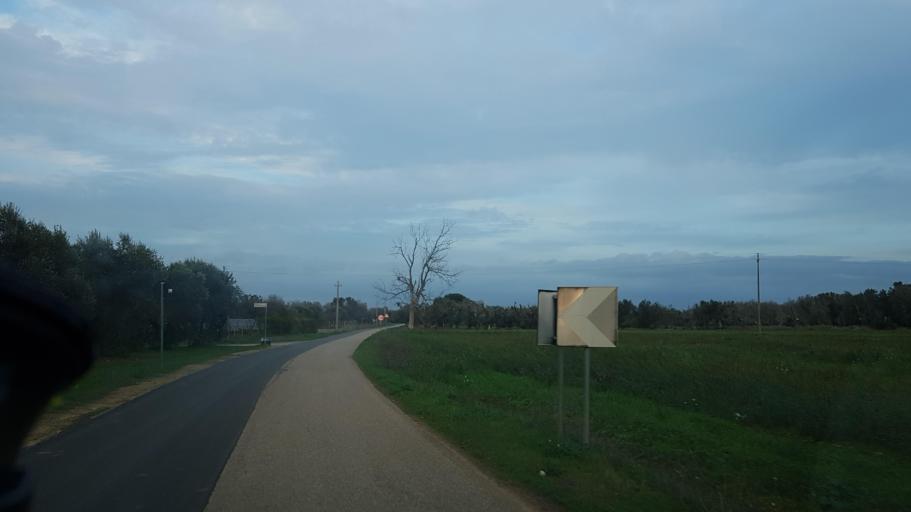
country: IT
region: Apulia
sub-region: Provincia di Brindisi
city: Mesagne
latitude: 40.5378
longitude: 17.7756
